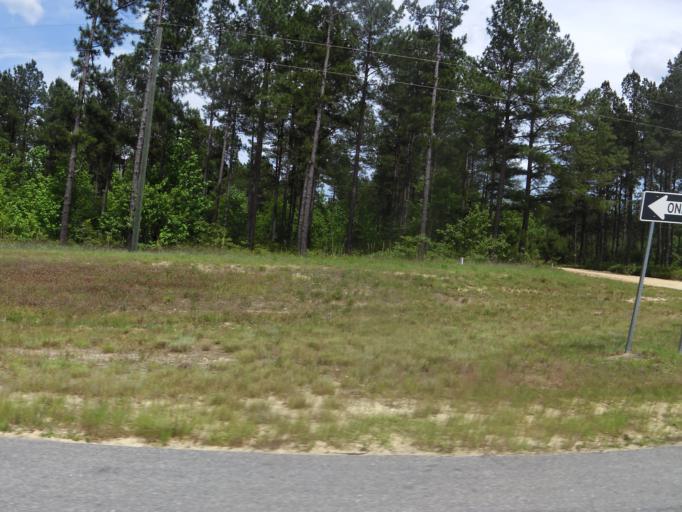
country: US
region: Georgia
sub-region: Emanuel County
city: Swainsboro
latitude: 32.7160
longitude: -82.3921
